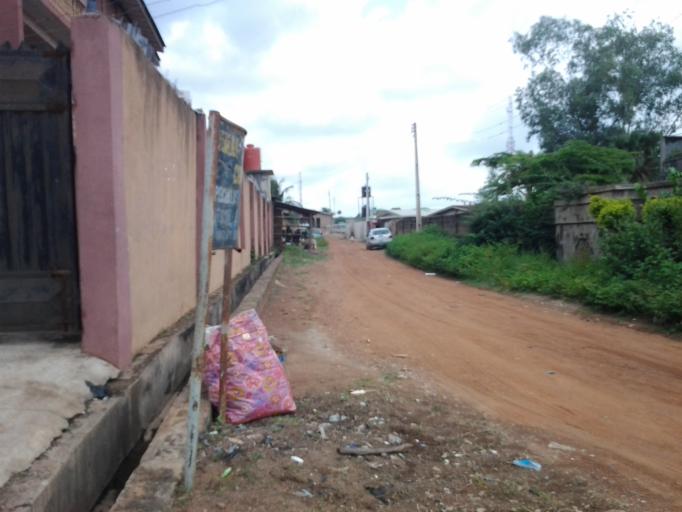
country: NG
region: Oyo
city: Ibadan
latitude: 7.4364
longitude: 3.9545
